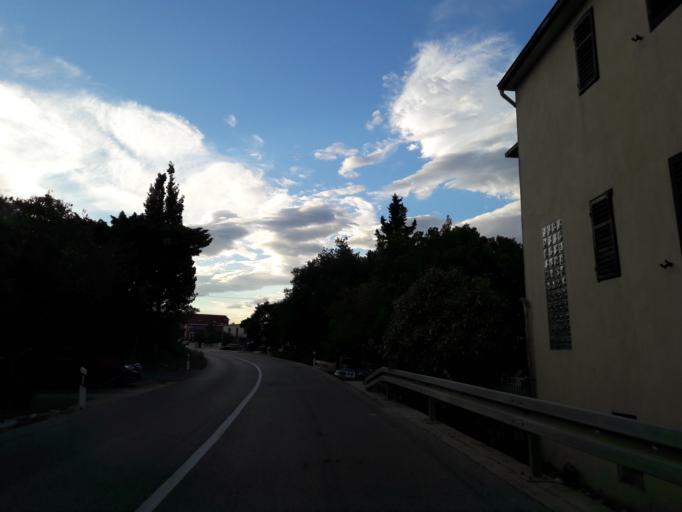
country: HR
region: Dubrovacko-Neretvanska
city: Komin
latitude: 42.9300
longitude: 17.4480
